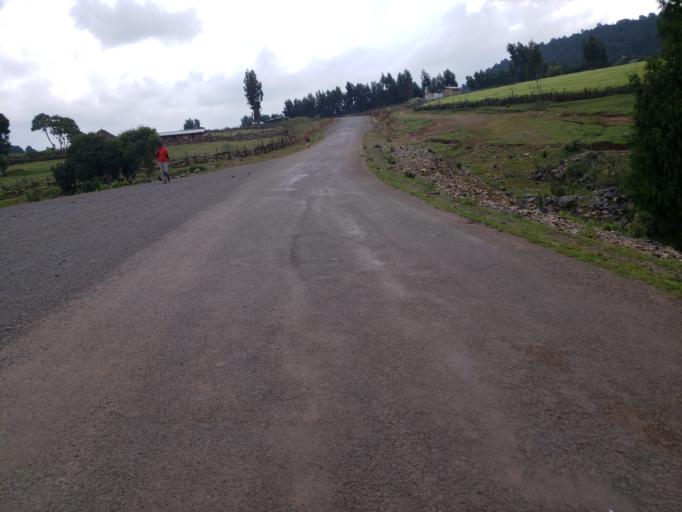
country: ET
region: Oromiya
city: Dodola
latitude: 6.8855
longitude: 39.3876
